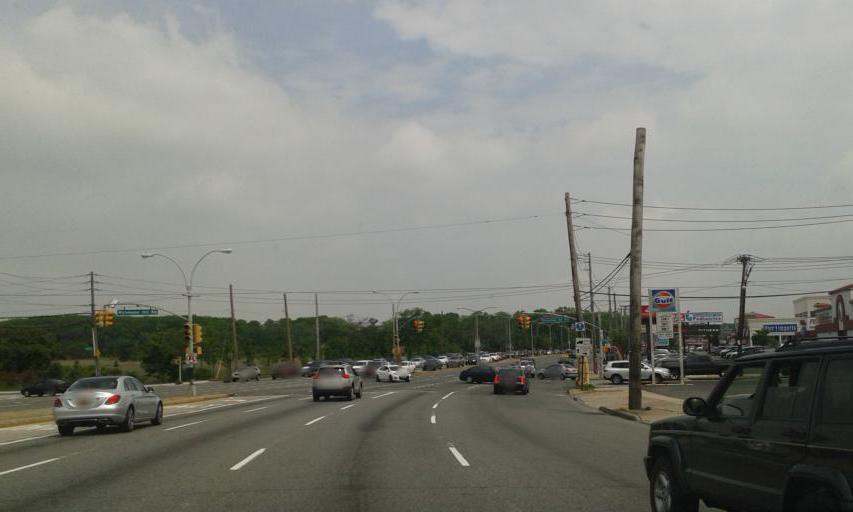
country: US
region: New York
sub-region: Richmond County
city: Bloomfield
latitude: 40.5880
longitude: -74.1679
